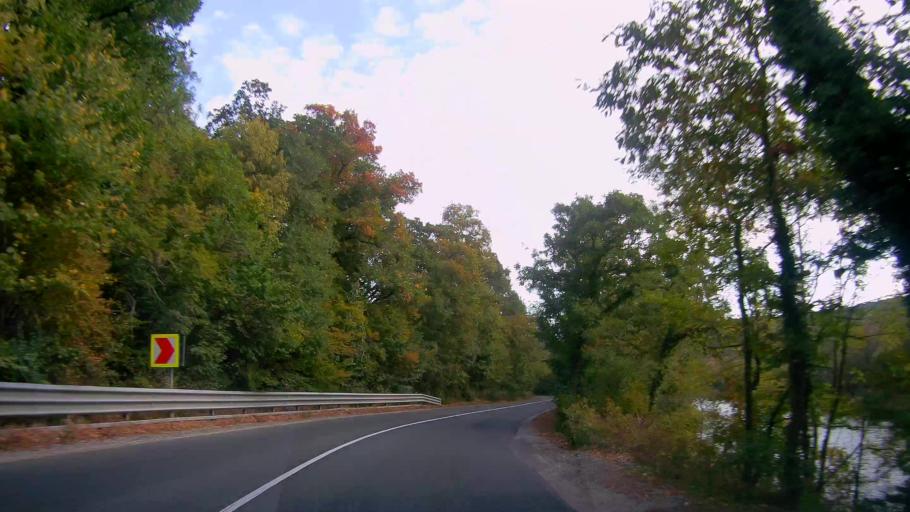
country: BG
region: Burgas
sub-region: Obshtina Primorsko
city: Primorsko
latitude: 42.3058
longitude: 27.7226
